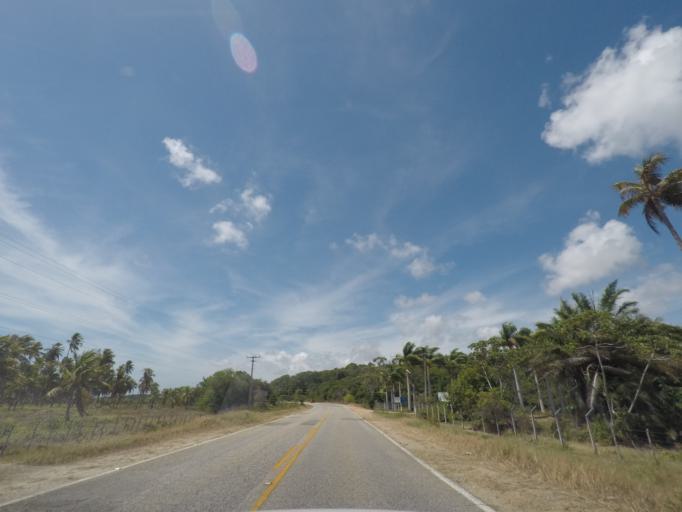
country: BR
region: Sergipe
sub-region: Sao Cristovao
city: Sao Cristovao
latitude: -11.1195
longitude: -37.1837
